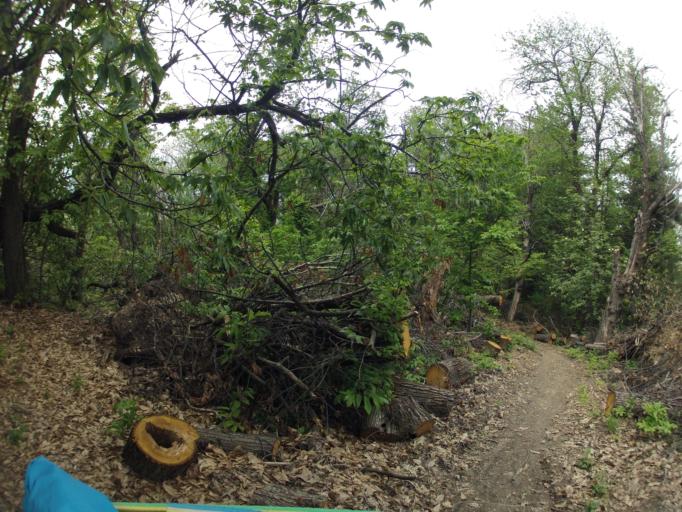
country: IT
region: Piedmont
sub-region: Provincia di Cuneo
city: Peveragno
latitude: 44.3313
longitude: 7.6001
